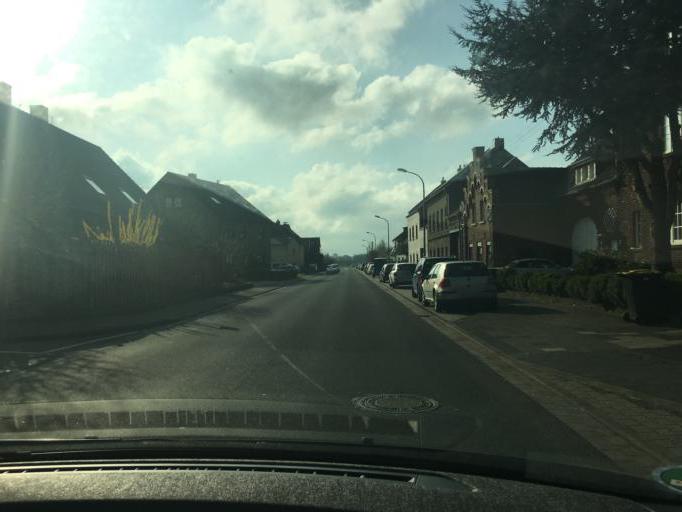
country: DE
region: North Rhine-Westphalia
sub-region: Regierungsbezirk Koln
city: Weilerswist
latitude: 50.7364
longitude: 6.8868
